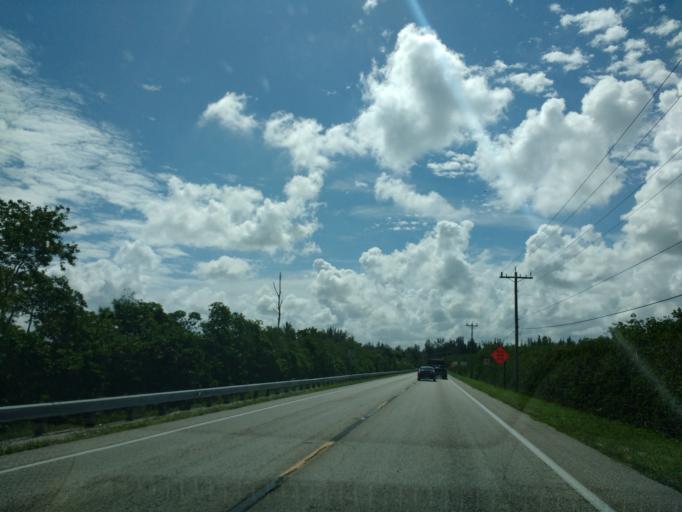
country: US
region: Florida
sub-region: Lee County
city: Pine Island Center
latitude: 26.6386
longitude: -82.0517
